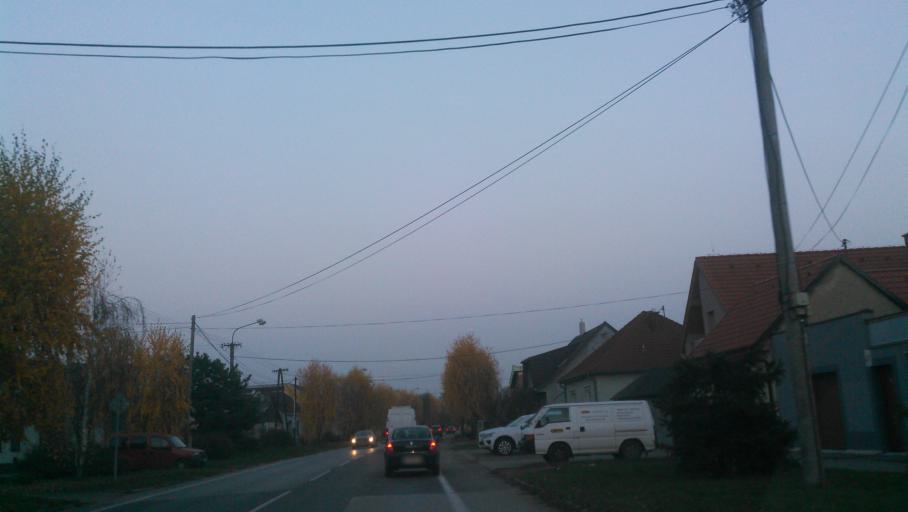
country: SK
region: Bratislavsky
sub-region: Okres Pezinok
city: Pezinok
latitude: 48.2824
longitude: 17.2632
